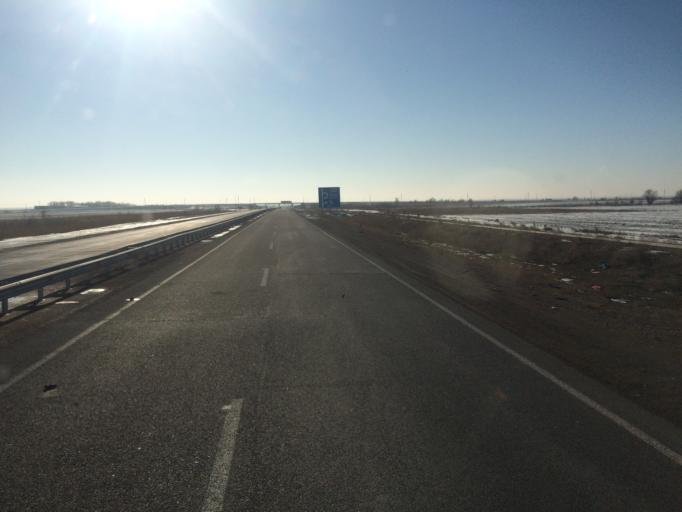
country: KG
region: Chuy
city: Sokuluk
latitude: 43.2836
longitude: 74.2374
